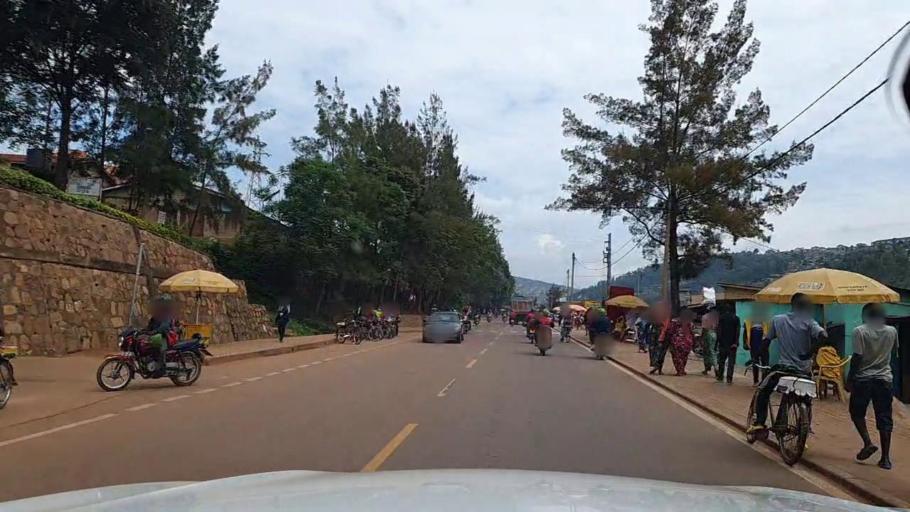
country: RW
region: Kigali
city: Kigali
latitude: -1.9293
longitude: 30.0460
